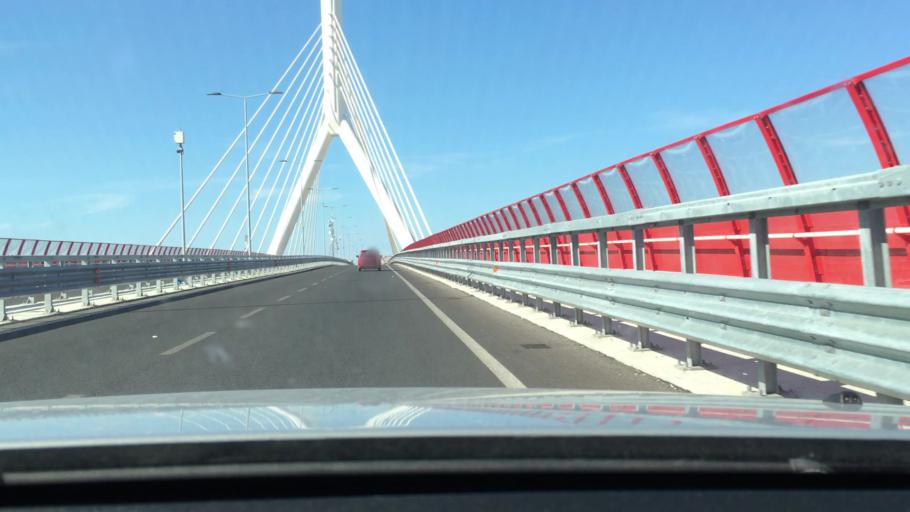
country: IT
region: Apulia
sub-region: Provincia di Bari
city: Bari
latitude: 41.1177
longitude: 16.8485
